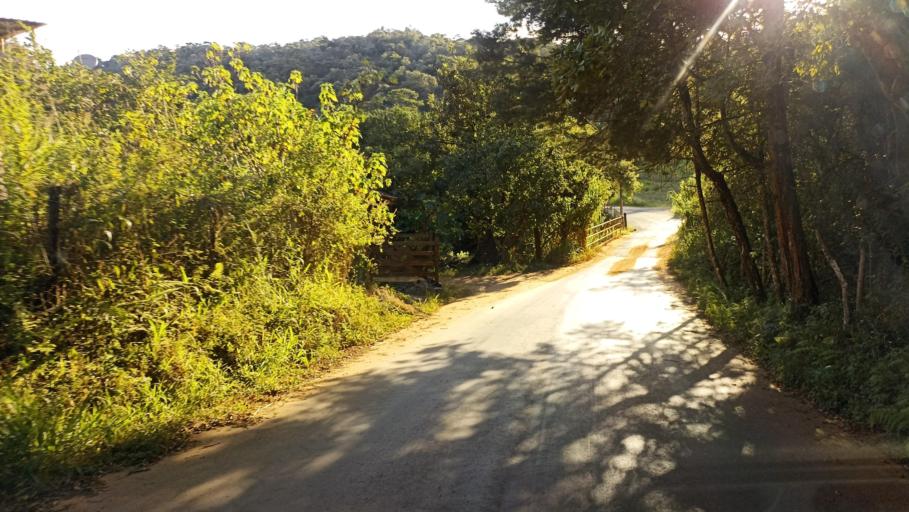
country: BR
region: Minas Gerais
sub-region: Ouro Preto
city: Ouro Preto
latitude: -20.3127
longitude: -43.6141
